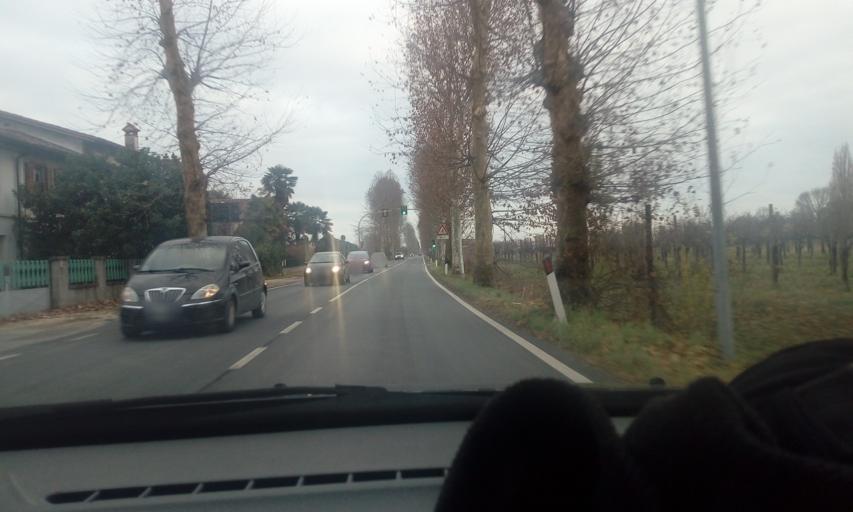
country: IT
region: Friuli Venezia Giulia
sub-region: Provincia di Udine
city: Terzo d'Aquileia
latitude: 45.7979
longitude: 13.3521
